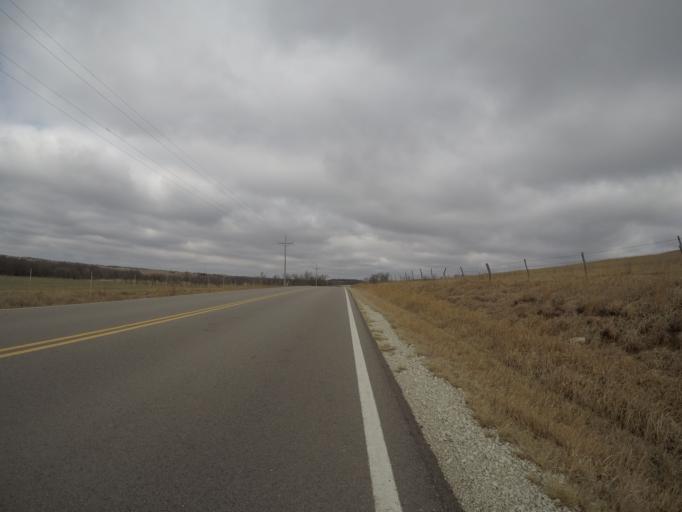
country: US
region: Kansas
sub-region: Pottawatomie County
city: Westmoreland
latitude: 39.4105
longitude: -96.4524
